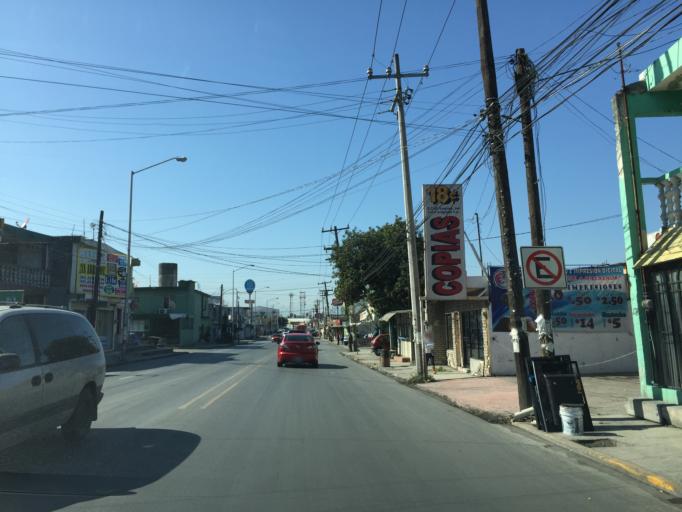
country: MX
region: Nuevo Leon
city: Guadalupe
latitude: 25.6829
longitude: -100.2311
